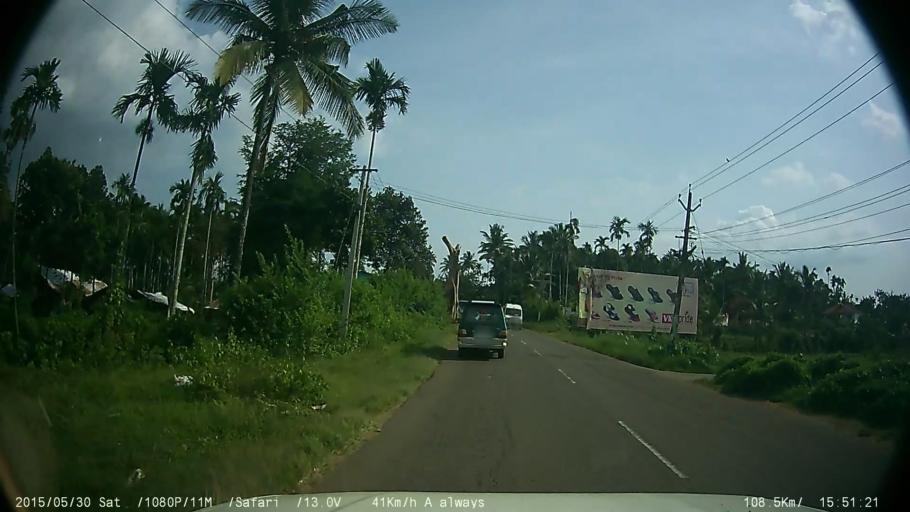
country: IN
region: Kerala
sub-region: Wayanad
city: Panamaram
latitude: 11.6817
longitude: 76.0751
